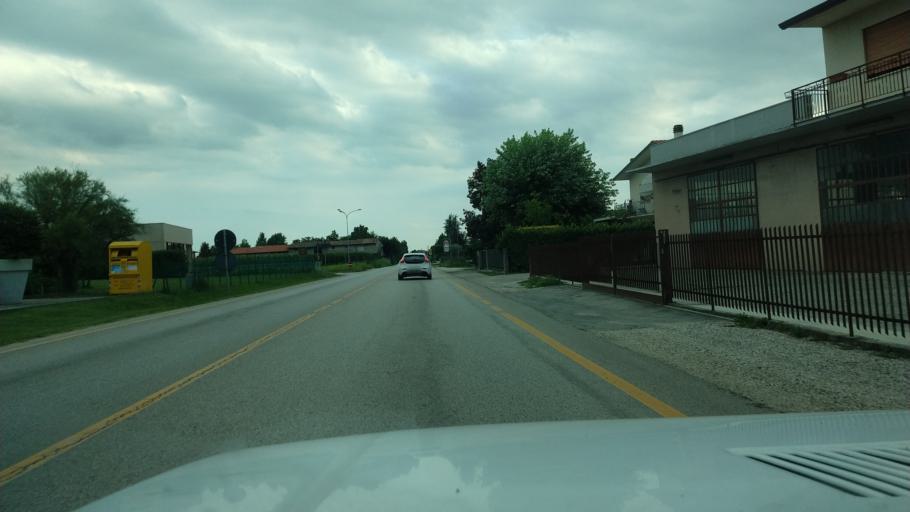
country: IT
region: Veneto
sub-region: Provincia di Vicenza
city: Marostica
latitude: 45.7245
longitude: 11.6513
